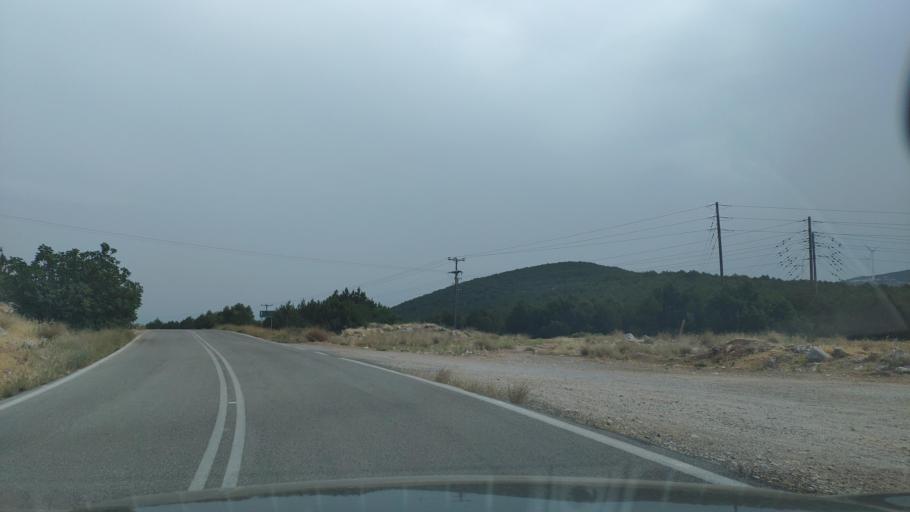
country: GR
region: Peloponnese
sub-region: Nomos Argolidos
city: Didyma
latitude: 37.5016
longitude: 23.1909
